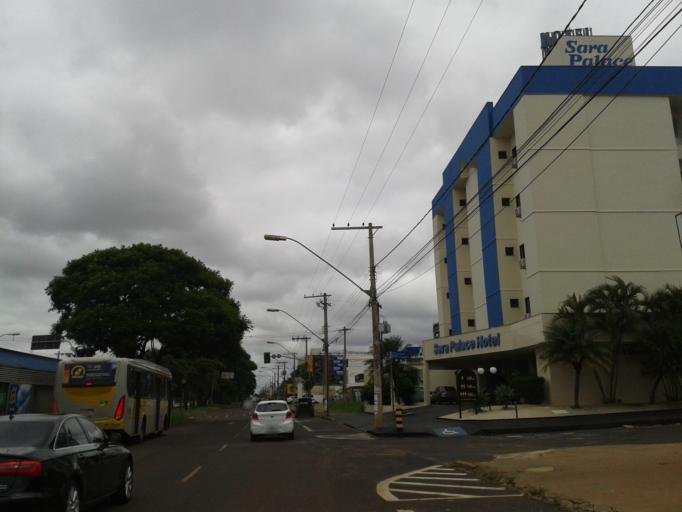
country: BR
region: Minas Gerais
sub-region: Uberlandia
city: Uberlandia
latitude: -18.9291
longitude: -48.2441
